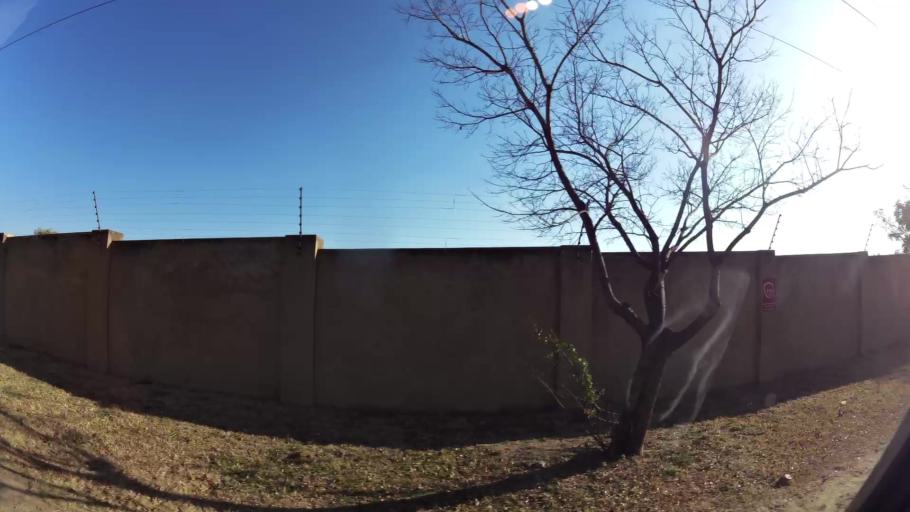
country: ZA
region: Gauteng
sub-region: City of Johannesburg Metropolitan Municipality
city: Diepsloot
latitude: -25.9989
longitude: 28.0410
